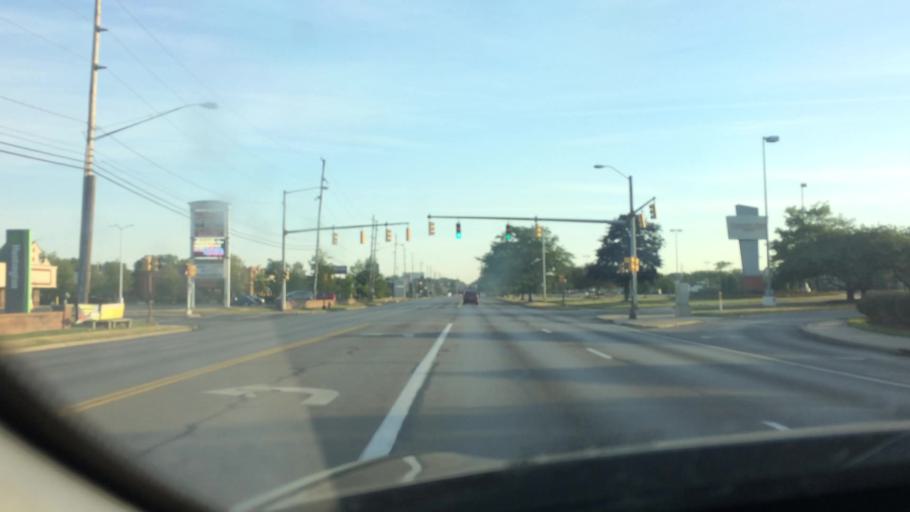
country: US
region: Ohio
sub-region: Lucas County
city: Ottawa Hills
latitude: 41.6930
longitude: -83.6447
